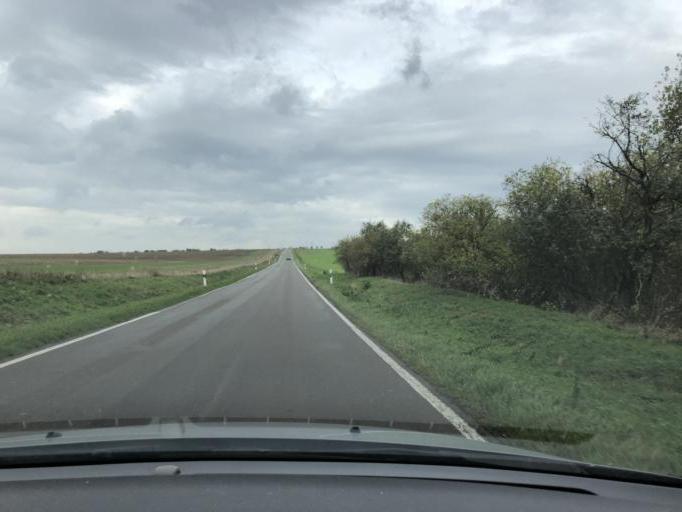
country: DE
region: Saxony-Anhalt
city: Uichteritz
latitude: 51.2121
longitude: 11.8955
